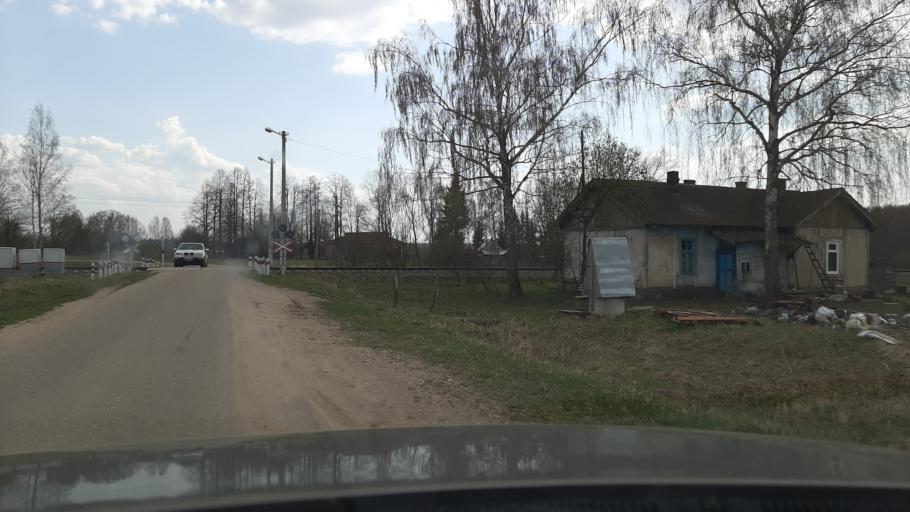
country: RU
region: Ivanovo
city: Furmanov
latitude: 57.3030
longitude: 41.1620
